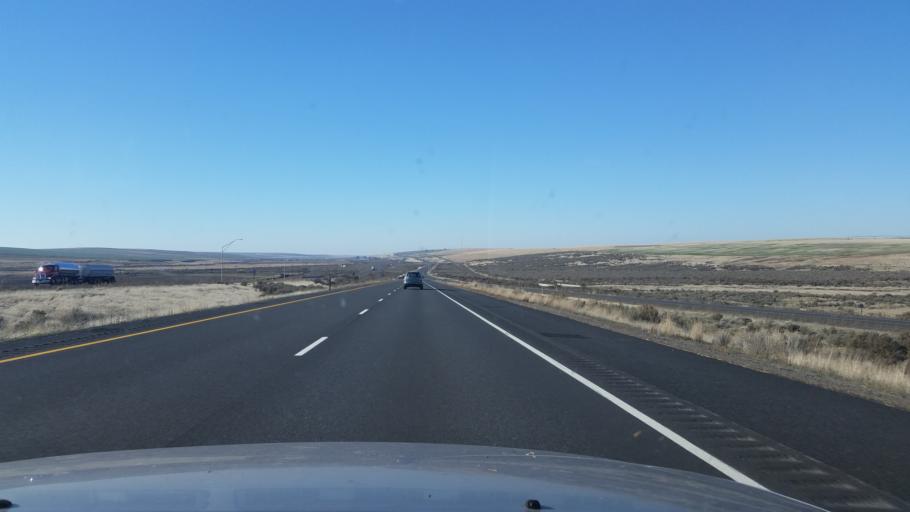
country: US
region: Washington
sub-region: Grant County
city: Warden
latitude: 47.0874
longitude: -118.8757
